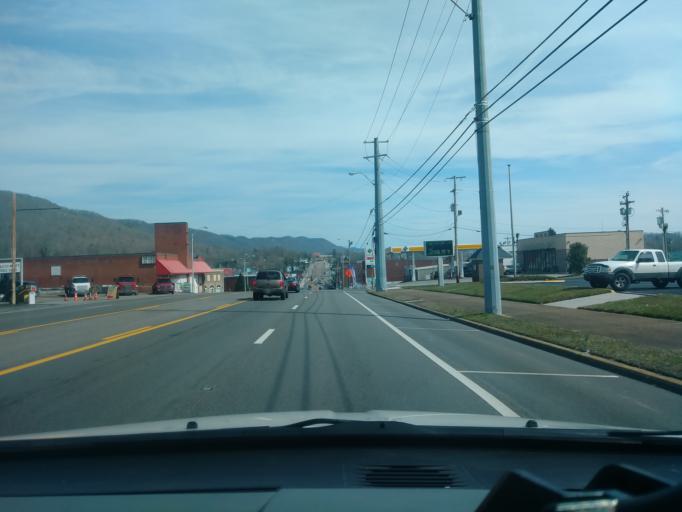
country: US
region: Tennessee
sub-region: Campbell County
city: LaFollette
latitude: 36.3805
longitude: -84.1228
